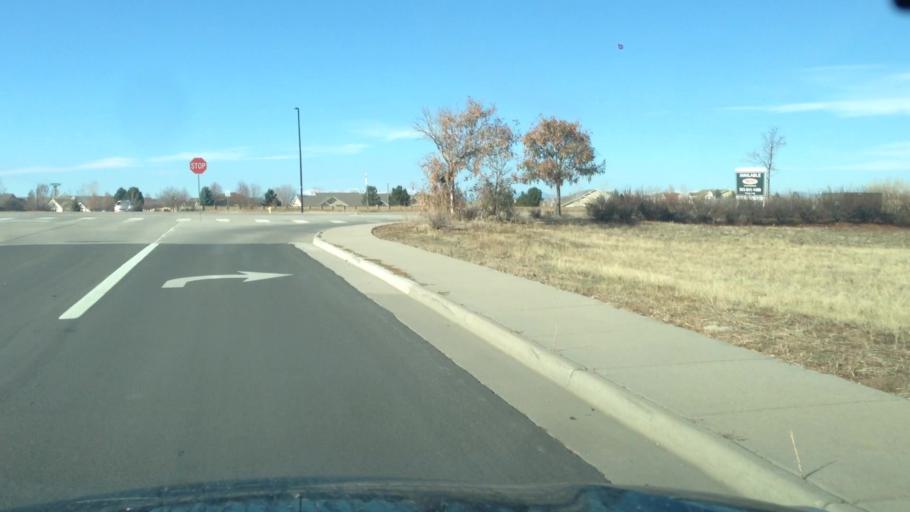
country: US
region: Colorado
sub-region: Douglas County
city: Stonegate
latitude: 39.5134
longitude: -104.7926
